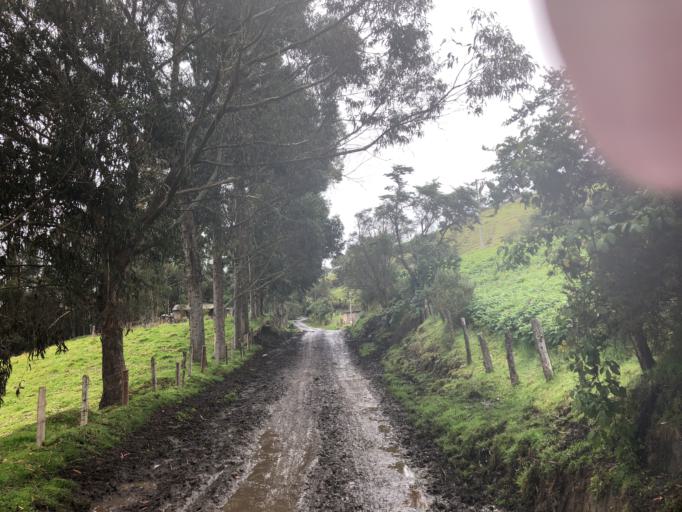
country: CO
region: Cauca
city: Totoro
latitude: 2.4732
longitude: -76.2977
